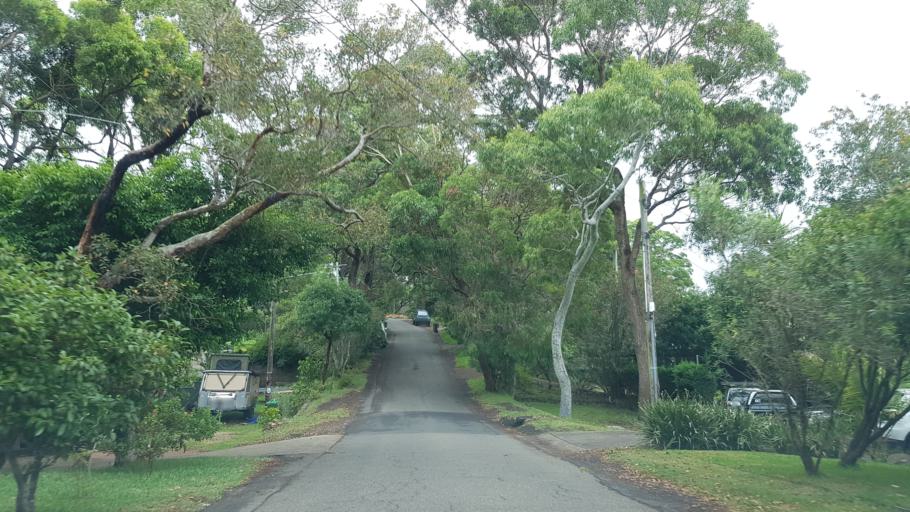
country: AU
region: New South Wales
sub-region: Pittwater
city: North Narrabeen
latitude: -33.7069
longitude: 151.2871
